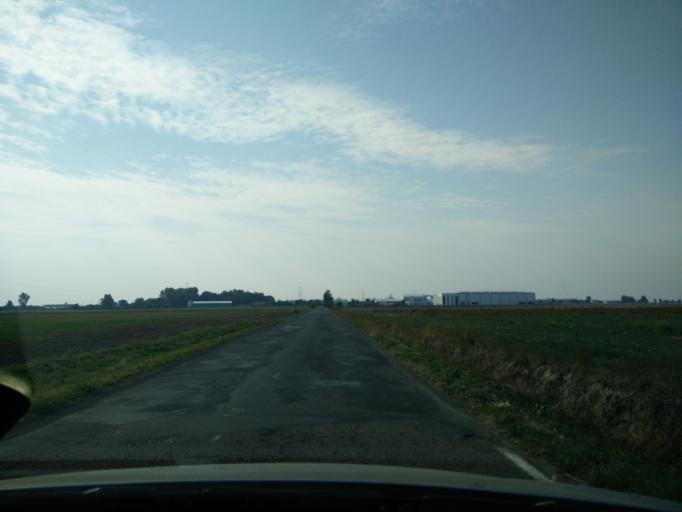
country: PL
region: Greater Poland Voivodeship
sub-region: Powiat sredzki
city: Dominowo
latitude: 52.3082
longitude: 17.2988
